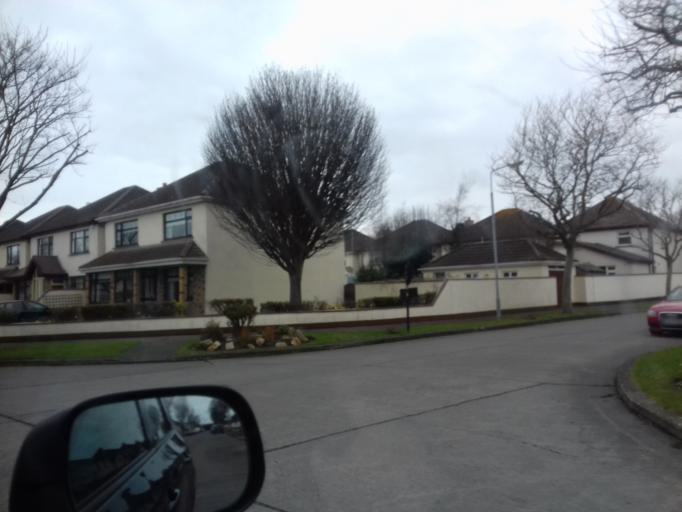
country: IE
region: Leinster
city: Portmarnock
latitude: 53.4345
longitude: -6.1340
